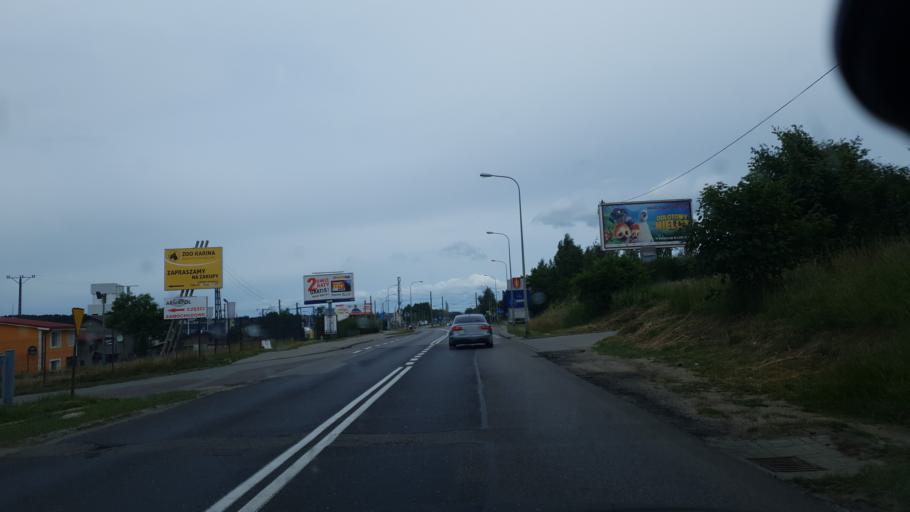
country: PL
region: Pomeranian Voivodeship
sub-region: Powiat kartuski
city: Chwaszczyno
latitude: 54.4559
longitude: 18.4479
